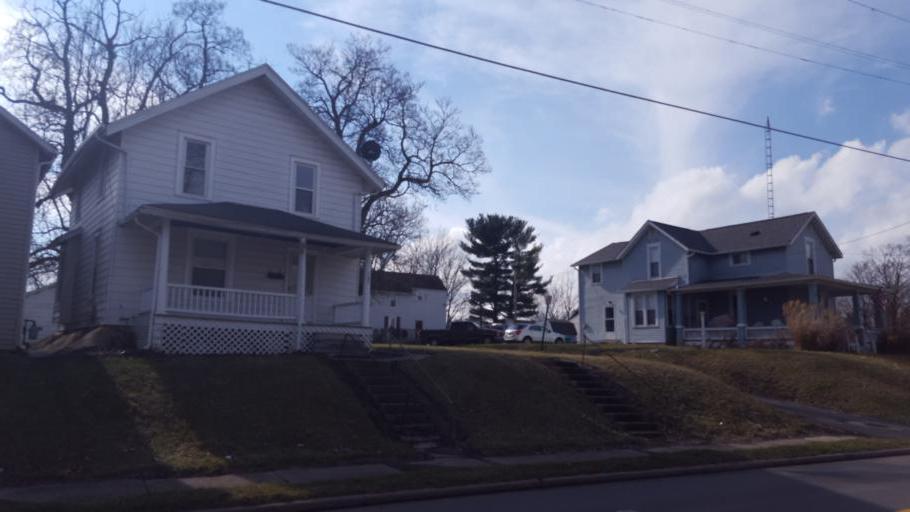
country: US
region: Ohio
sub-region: Richland County
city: Mansfield
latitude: 40.7704
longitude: -82.5266
